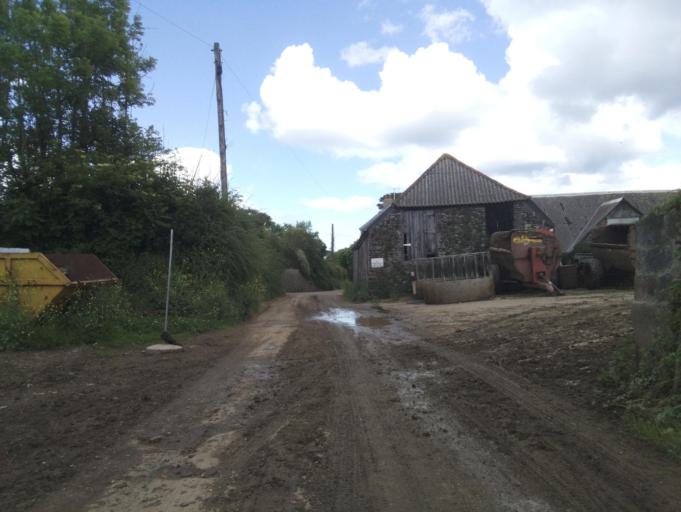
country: GB
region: England
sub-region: Devon
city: Dartmouth
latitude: 50.3575
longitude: -3.5485
